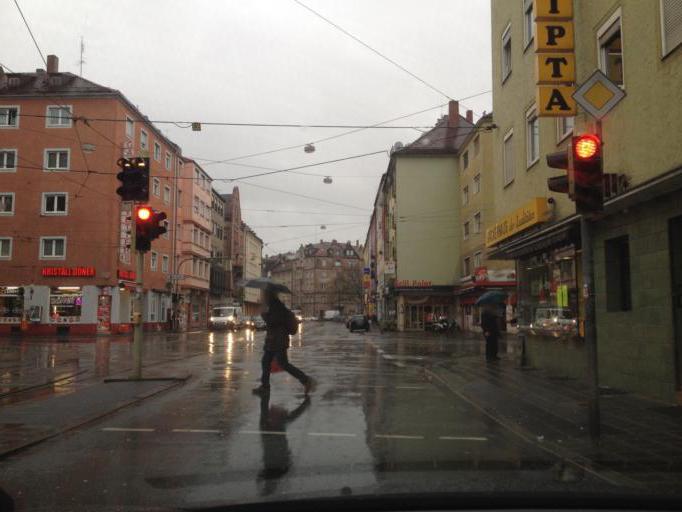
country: DE
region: Bavaria
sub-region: Regierungsbezirk Mittelfranken
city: Nuernberg
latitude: 49.4398
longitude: 11.0671
